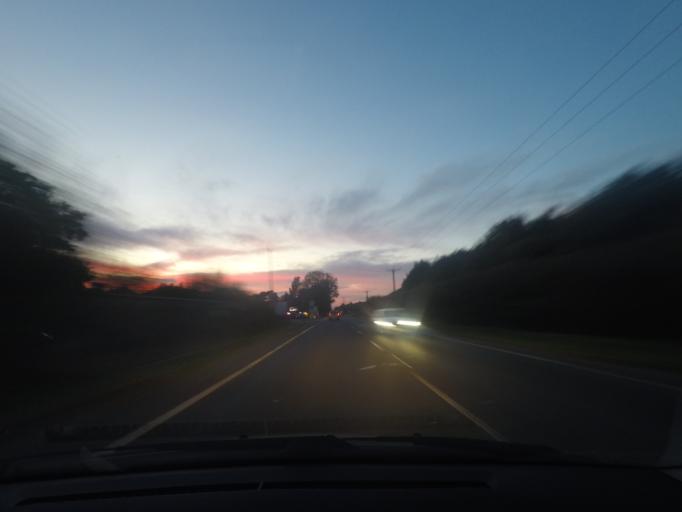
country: GB
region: England
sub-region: East Riding of Yorkshire
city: Thornton
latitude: 53.9361
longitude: -0.8530
